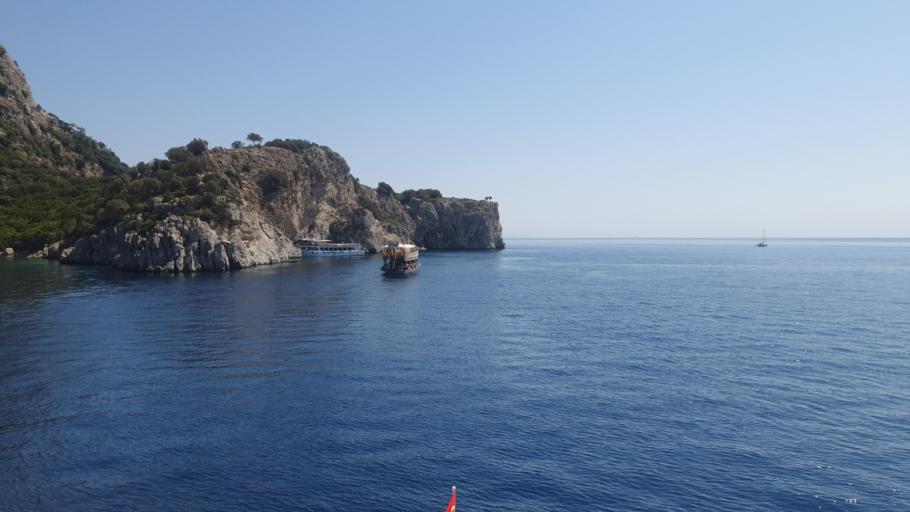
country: TR
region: Mugla
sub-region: Marmaris
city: Marmaris
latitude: 36.7924
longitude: 28.2814
